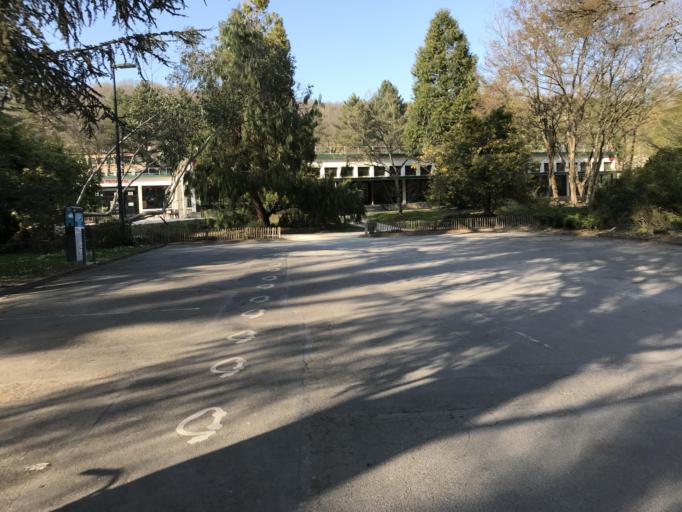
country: FR
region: Ile-de-France
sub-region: Departement de l'Essonne
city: Bures-sur-Yvette
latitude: 48.7020
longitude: 2.1793
